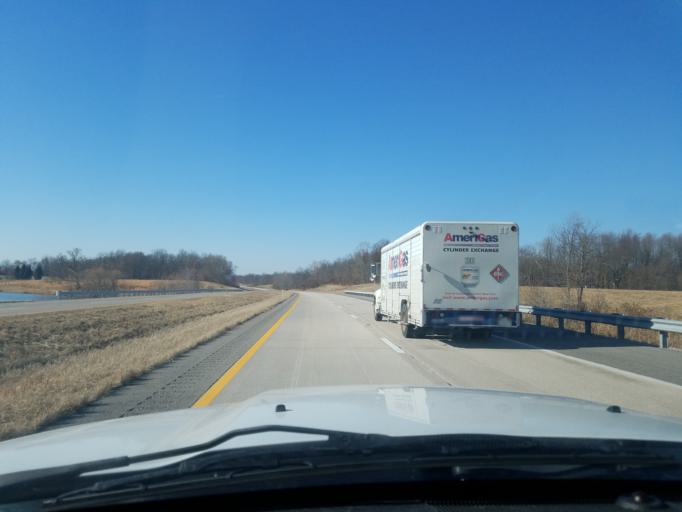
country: US
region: Kentucky
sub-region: Henderson County
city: Henderson
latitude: 37.7723
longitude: -87.4324
